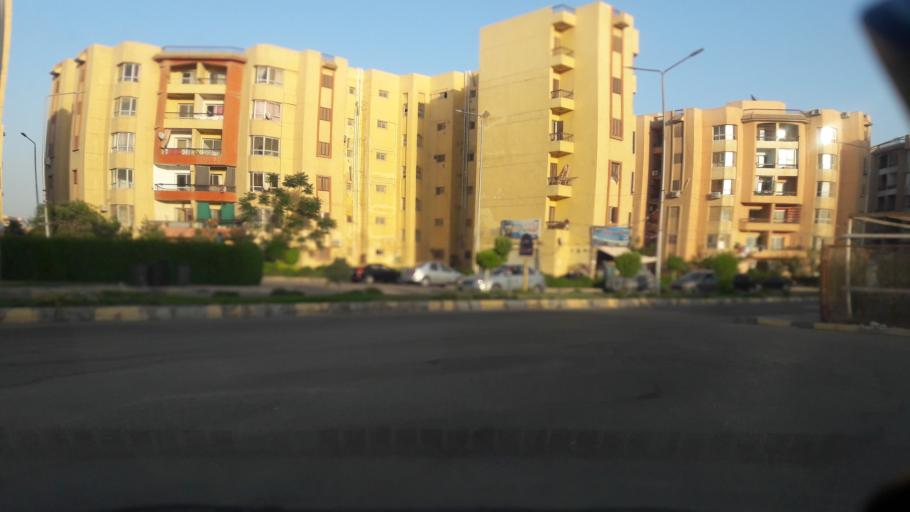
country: EG
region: Al Jizah
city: Madinat Sittah Uktubar
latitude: 29.9554
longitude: 31.0458
